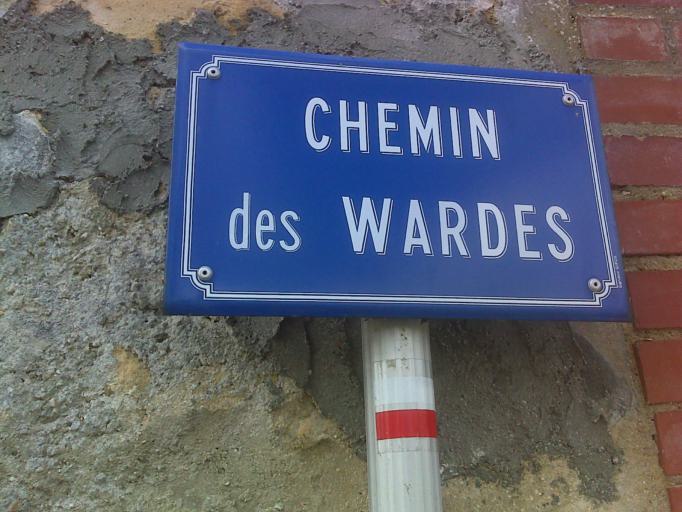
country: FR
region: Champagne-Ardenne
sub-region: Departement de la Marne
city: Rilly-la-Montagne
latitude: 49.1628
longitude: 4.0495
